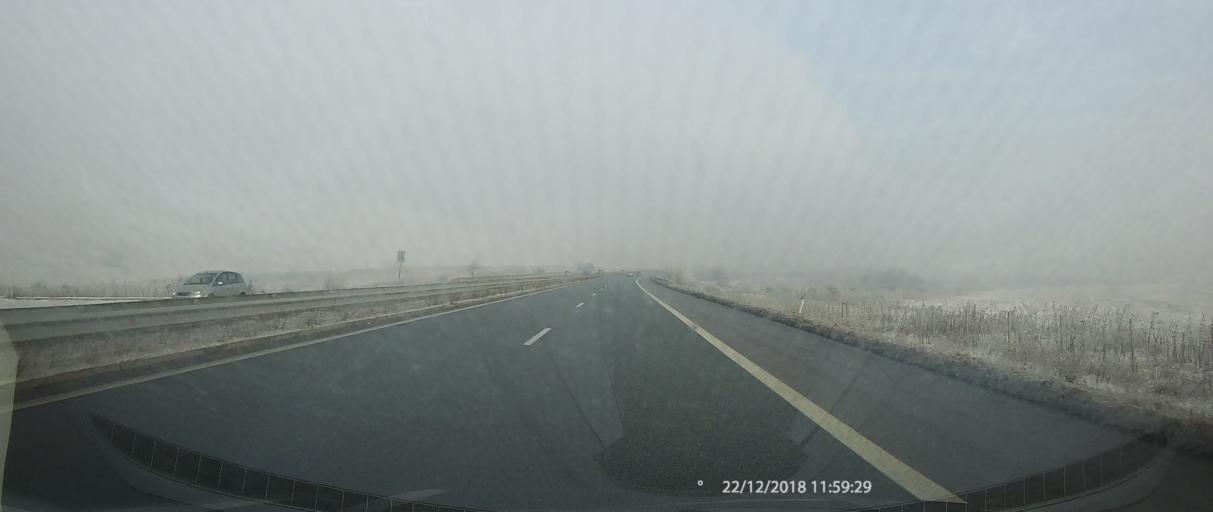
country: BG
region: Sofiya
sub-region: Obshtina Bozhurishte
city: Bozhurishte
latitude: 42.7044
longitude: 23.2117
